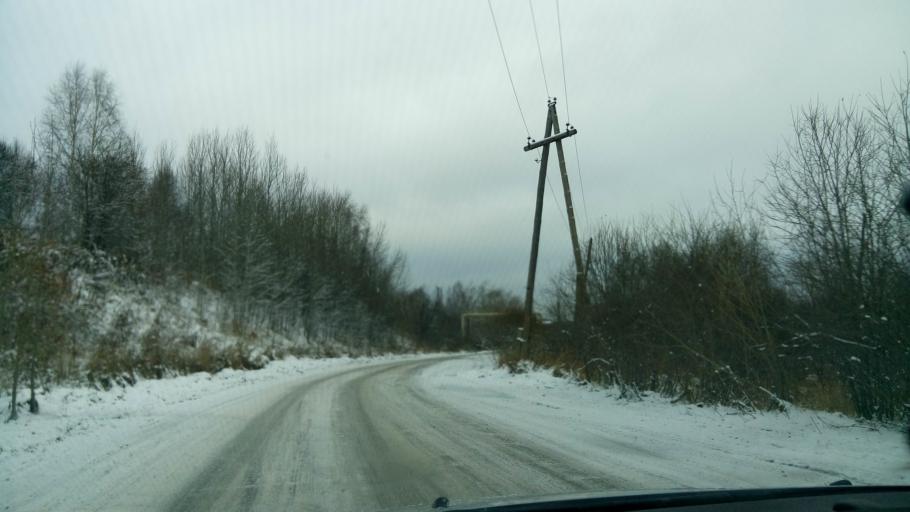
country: RU
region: Sverdlovsk
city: Polevskoy
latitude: 56.4608
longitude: 60.1820
